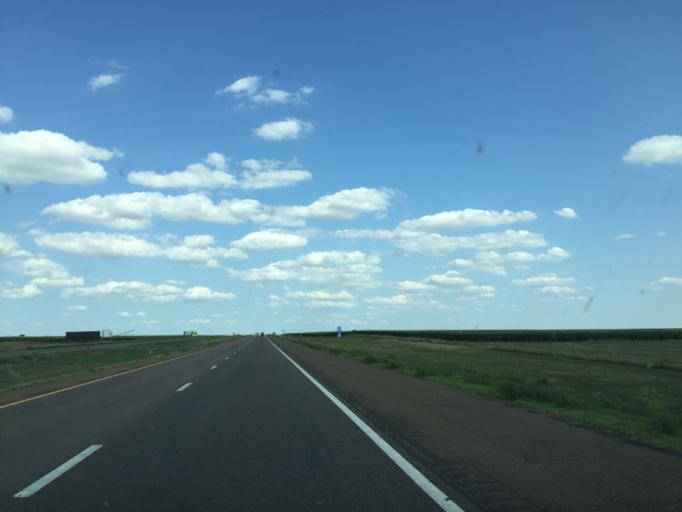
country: US
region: Kansas
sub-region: Gove County
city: Gove
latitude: 39.1082
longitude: -100.4735
